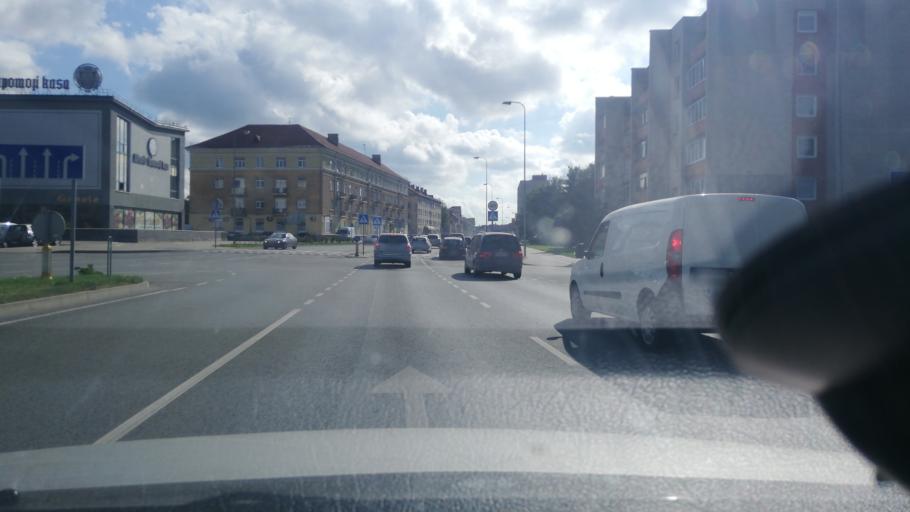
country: LT
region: Klaipedos apskritis
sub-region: Klaipeda
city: Klaipeda
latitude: 55.6828
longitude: 21.1501
